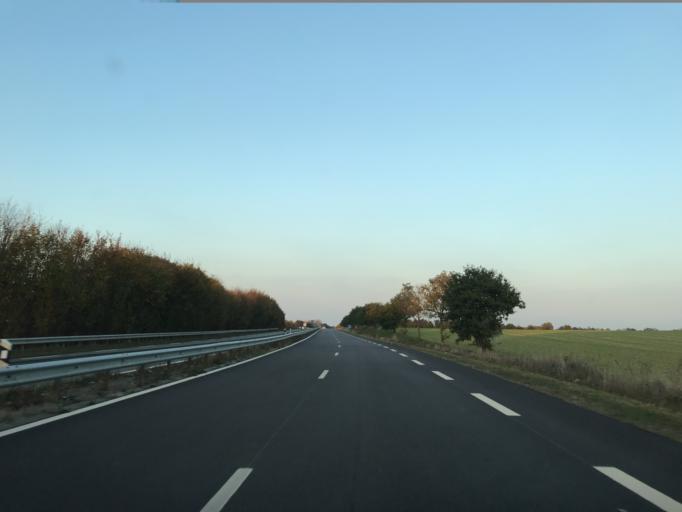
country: FR
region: Haute-Normandie
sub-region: Departement de l'Eure
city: Bourth
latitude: 48.6694
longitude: 0.7875
